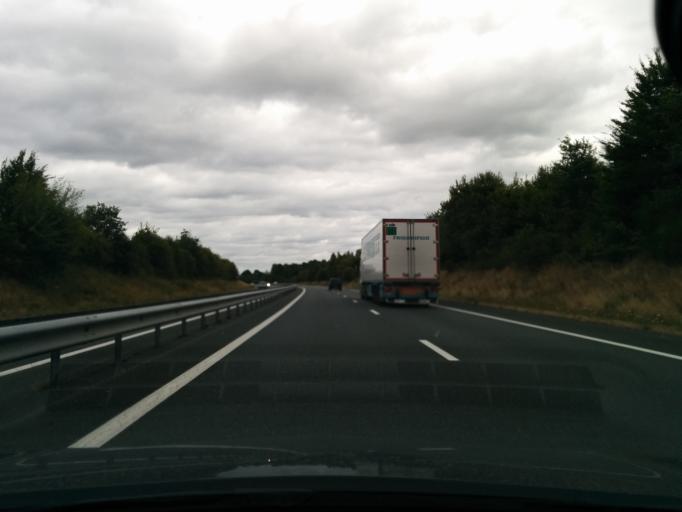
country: FR
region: Centre
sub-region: Departement de l'Indre
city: Chantome
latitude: 46.4165
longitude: 1.4686
